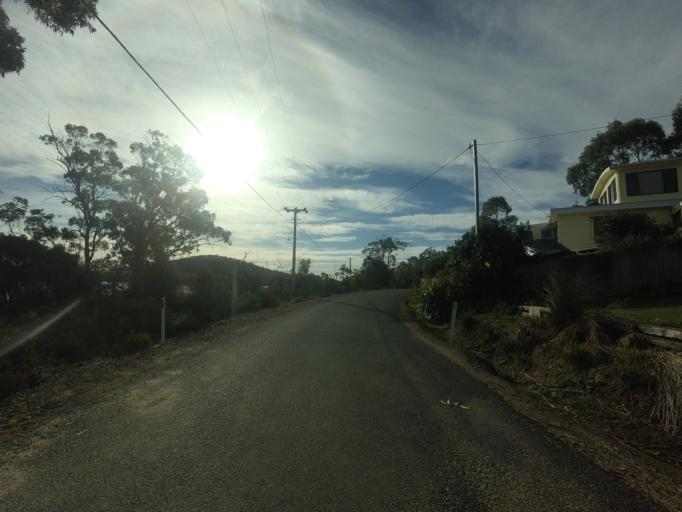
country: AU
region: Tasmania
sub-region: Sorell
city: Sorell
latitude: -42.9774
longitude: 147.8375
